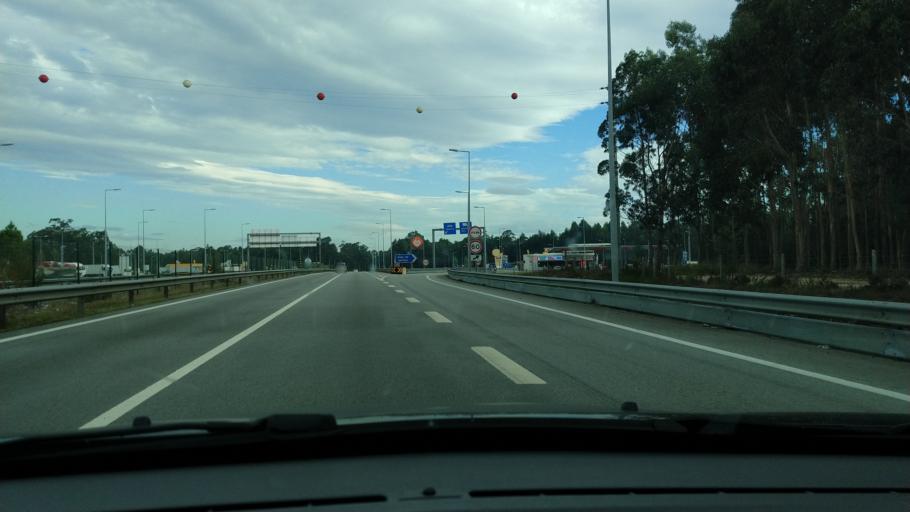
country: PT
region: Aveiro
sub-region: Aveiro
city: Eixo
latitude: 40.6585
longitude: -8.5923
